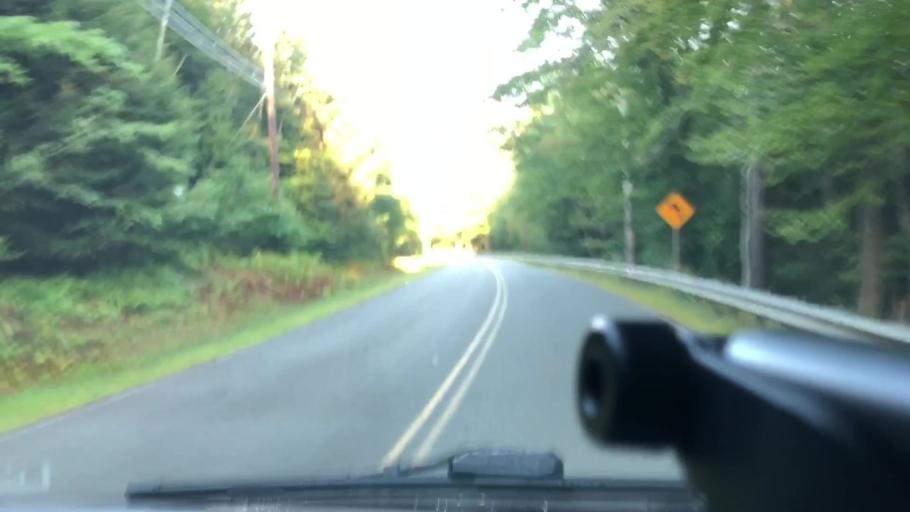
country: US
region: Massachusetts
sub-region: Franklin County
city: Ashfield
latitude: 42.5098
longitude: -72.8344
